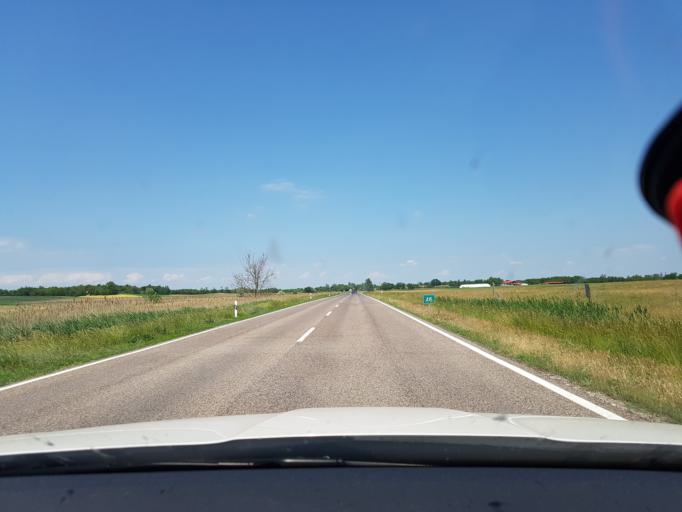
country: HU
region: Hajdu-Bihar
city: Egyek
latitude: 47.5812
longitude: 20.8541
